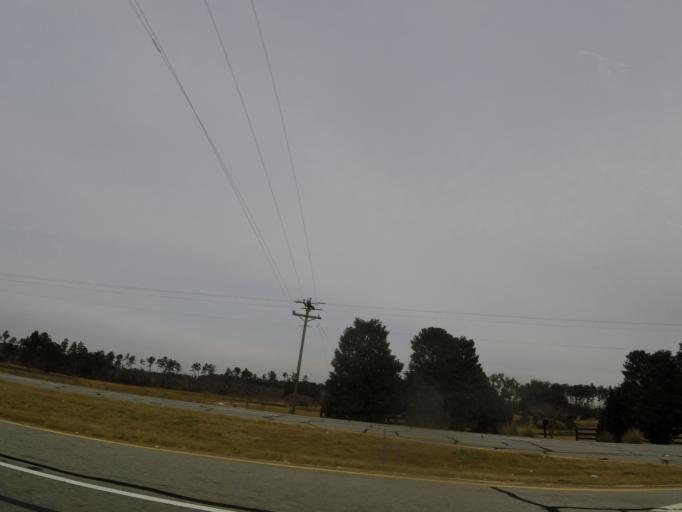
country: US
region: Georgia
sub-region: Decatur County
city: Bainbridge
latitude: 30.9531
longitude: -84.7082
